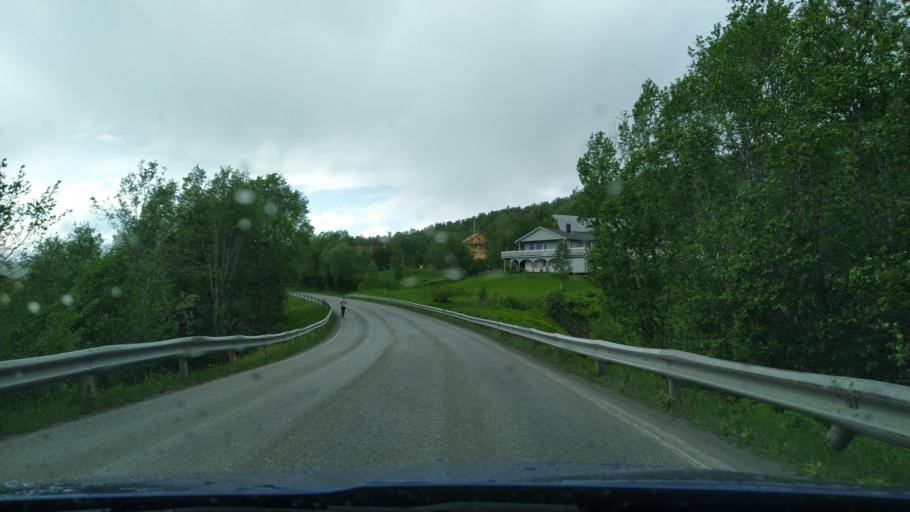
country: NO
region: Troms
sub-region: Sorreisa
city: Sorreisa
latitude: 69.1582
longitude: 18.1588
